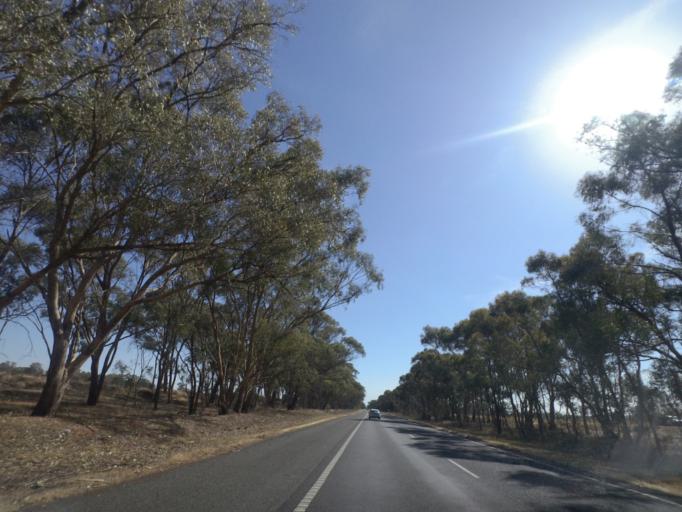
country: AU
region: Victoria
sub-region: Greater Shepparton
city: Shepparton
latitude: -36.6900
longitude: 145.2228
